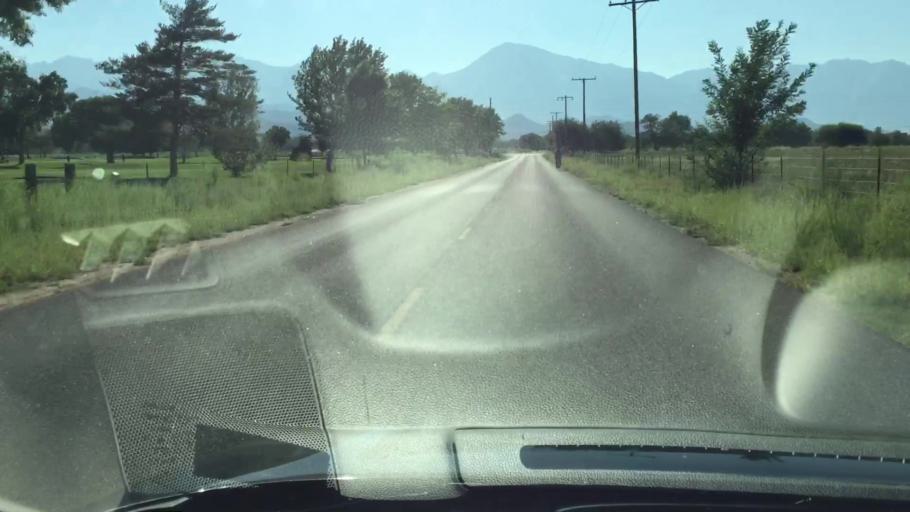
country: US
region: California
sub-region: Inyo County
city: Bishop
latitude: 37.3468
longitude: -118.4017
